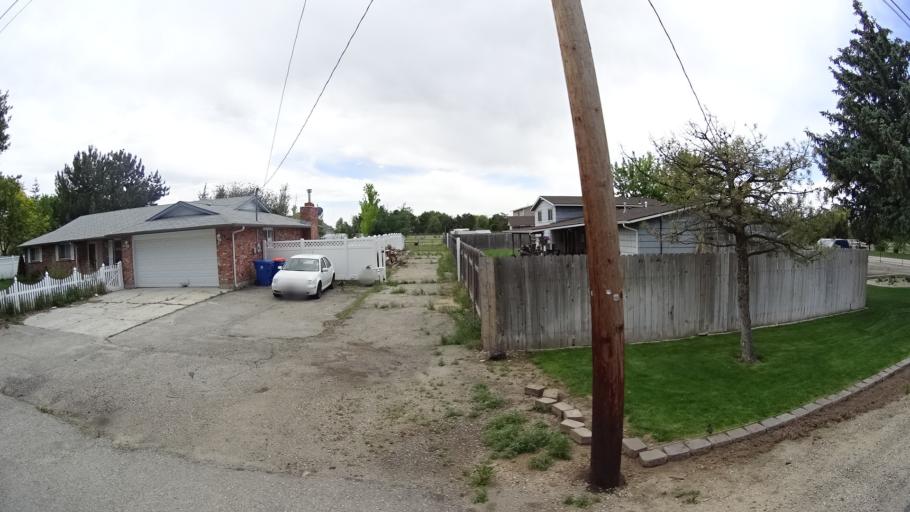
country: US
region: Idaho
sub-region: Ada County
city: Meridian
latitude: 43.5757
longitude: -116.3415
